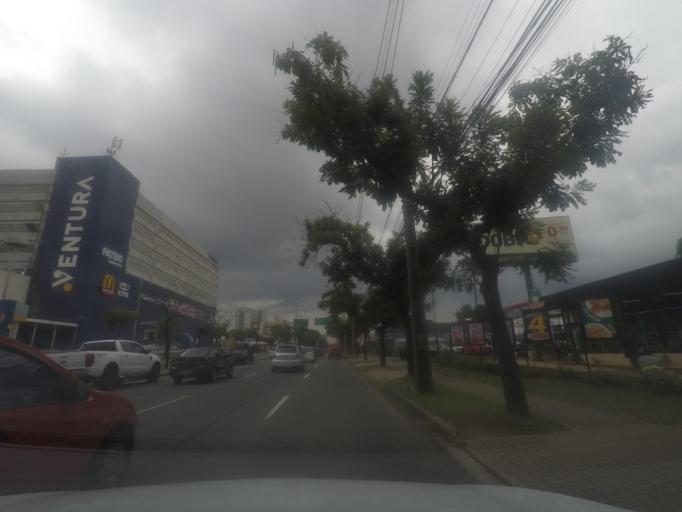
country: BR
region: Parana
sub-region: Curitiba
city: Curitiba
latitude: -25.4783
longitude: -49.2957
